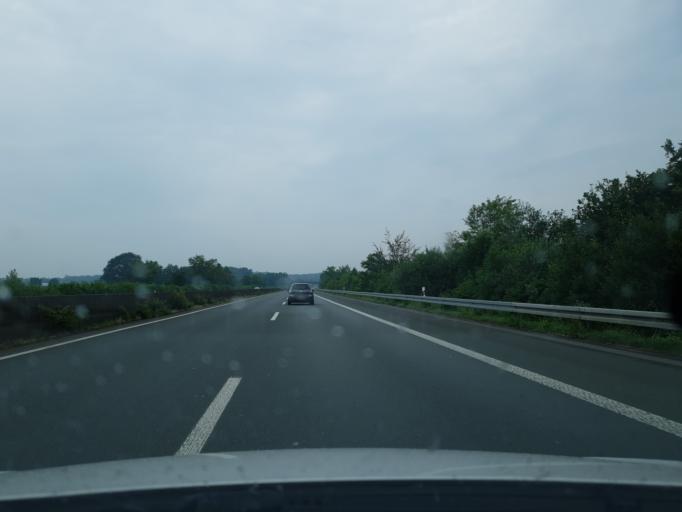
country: DE
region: North Rhine-Westphalia
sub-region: Regierungsbezirk Munster
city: Velen
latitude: 51.8642
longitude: 7.0071
